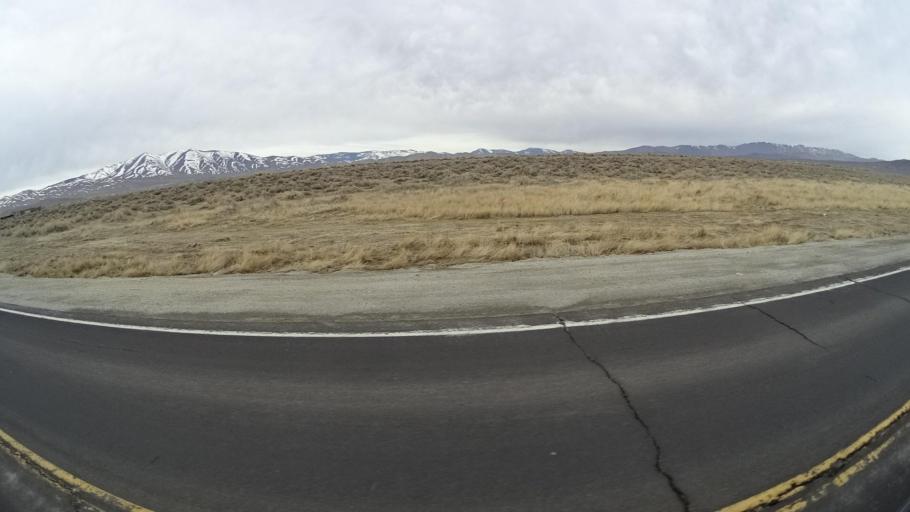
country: US
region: Nevada
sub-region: Washoe County
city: Lemmon Valley
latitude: 39.6537
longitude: -119.8284
